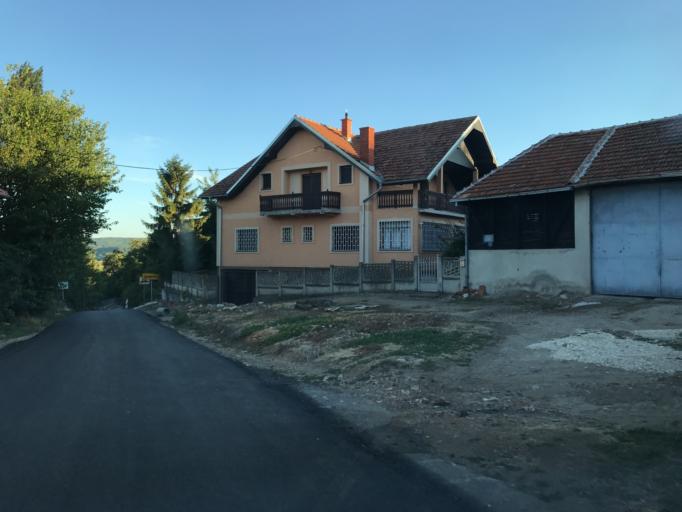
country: BG
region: Vidin
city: Bregovo
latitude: 44.1236
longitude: 22.5987
